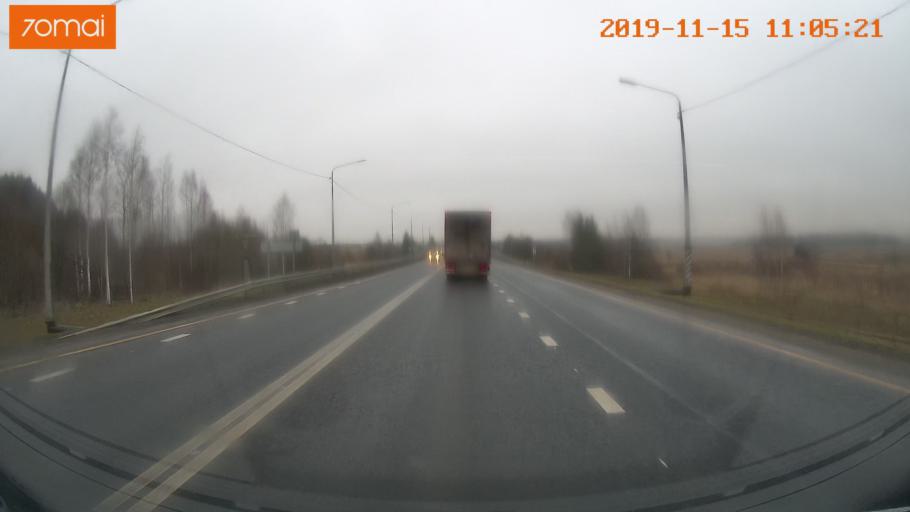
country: RU
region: Vologda
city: Chebsara
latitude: 59.1185
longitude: 39.0026
